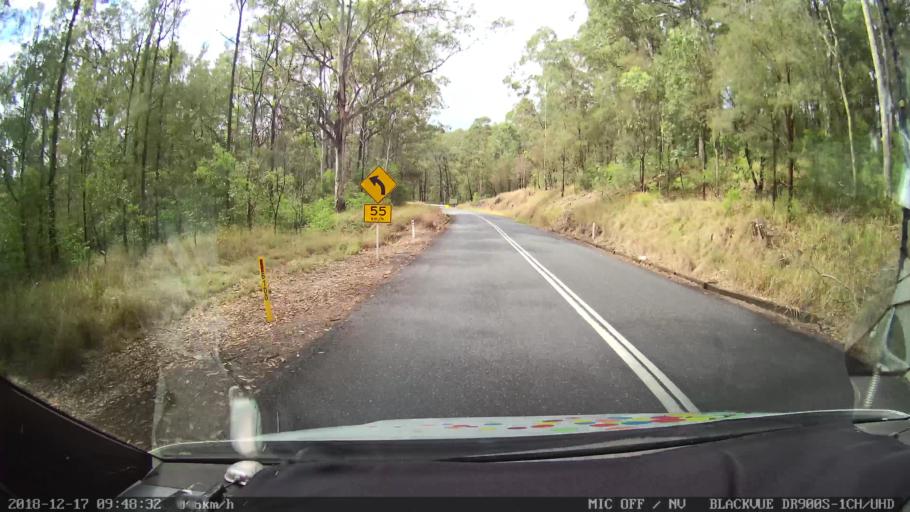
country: AU
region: New South Wales
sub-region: Tenterfield Municipality
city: Carrolls Creek
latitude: -28.9248
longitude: 152.3443
